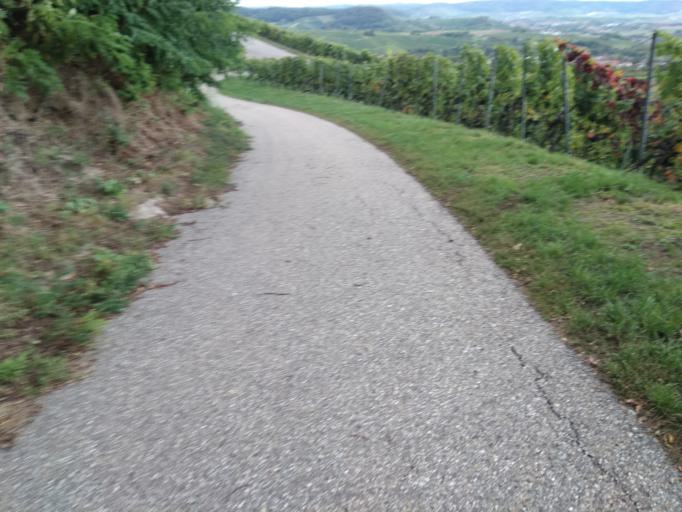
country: DE
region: Baden-Wuerttemberg
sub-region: Regierungsbezirk Stuttgart
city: Eberstadt
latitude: 49.1652
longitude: 9.3135
